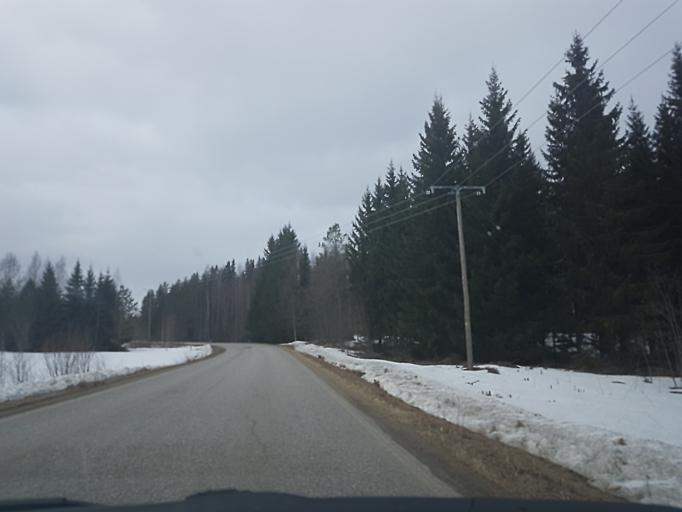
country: FI
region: Northern Savo
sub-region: Koillis-Savo
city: Kaavi
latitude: 63.0098
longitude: 28.6651
